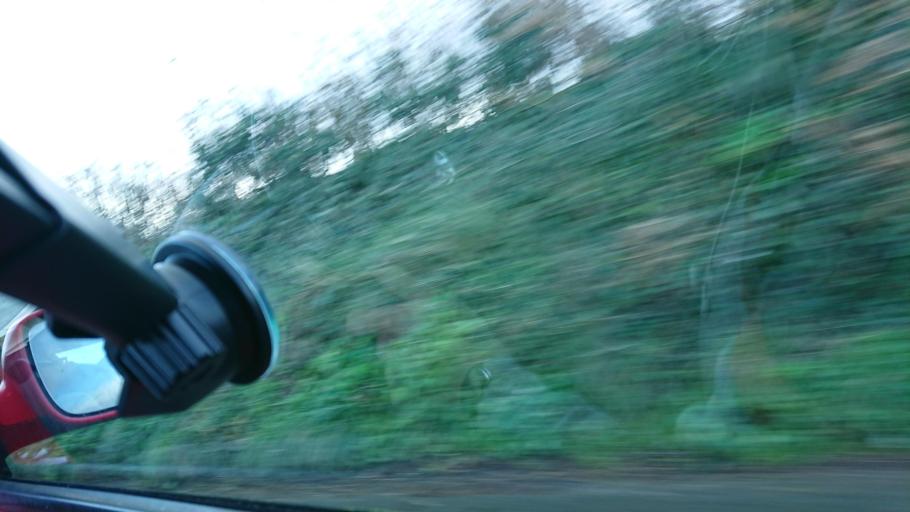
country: GB
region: England
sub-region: Cornwall
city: Looe
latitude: 50.3486
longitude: -4.4782
